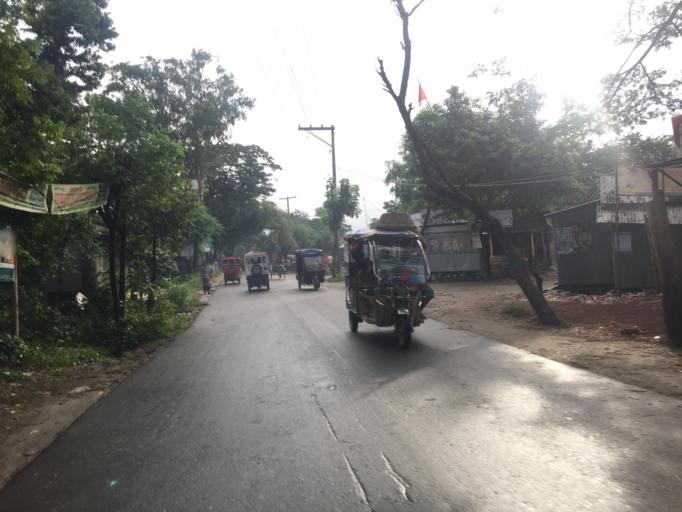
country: BD
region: Dhaka
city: Narayanganj
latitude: 23.5537
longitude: 90.5039
